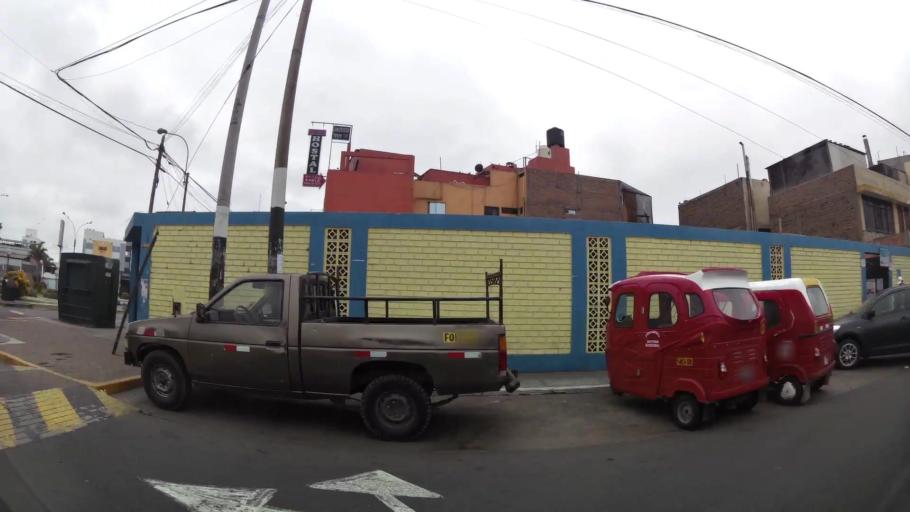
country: PE
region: Callao
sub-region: Callao
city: Callao
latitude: -12.0564
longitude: -77.0960
